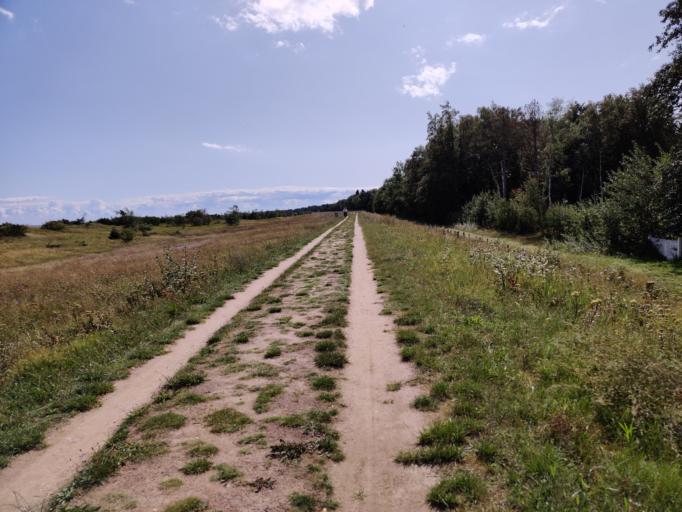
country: DK
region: Zealand
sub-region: Guldborgsund Kommune
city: Nykobing Falster
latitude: 54.6755
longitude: 11.9622
